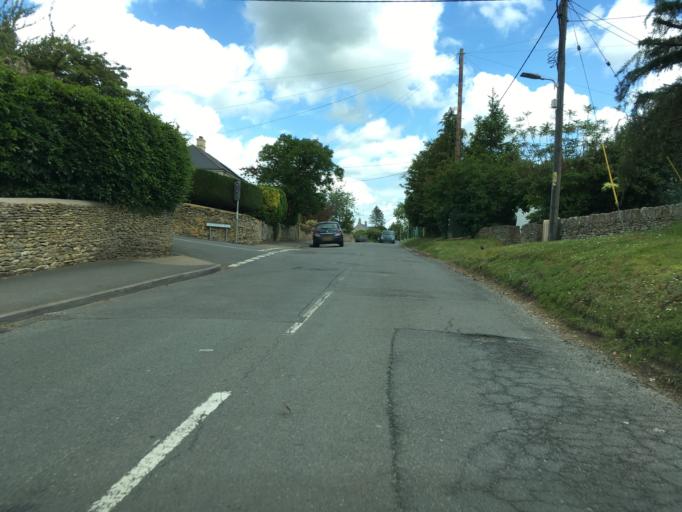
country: GB
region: England
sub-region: Gloucestershire
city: Tetbury
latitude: 51.6399
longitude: -2.1540
